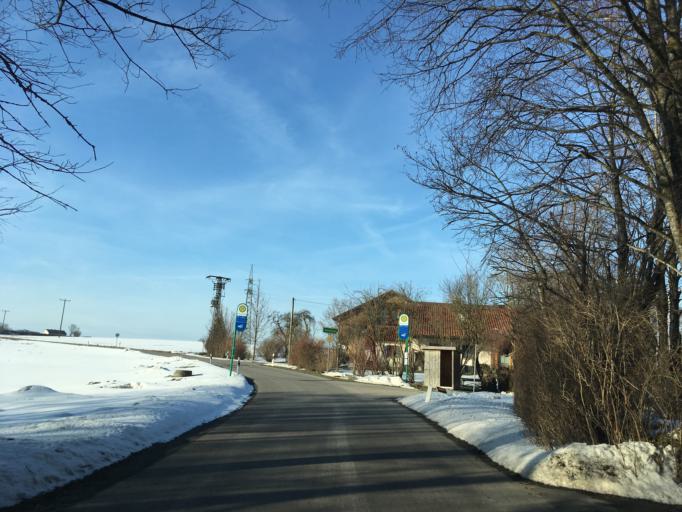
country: DE
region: Bavaria
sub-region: Upper Bavaria
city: Steinhoring
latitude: 48.1056
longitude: 12.0619
